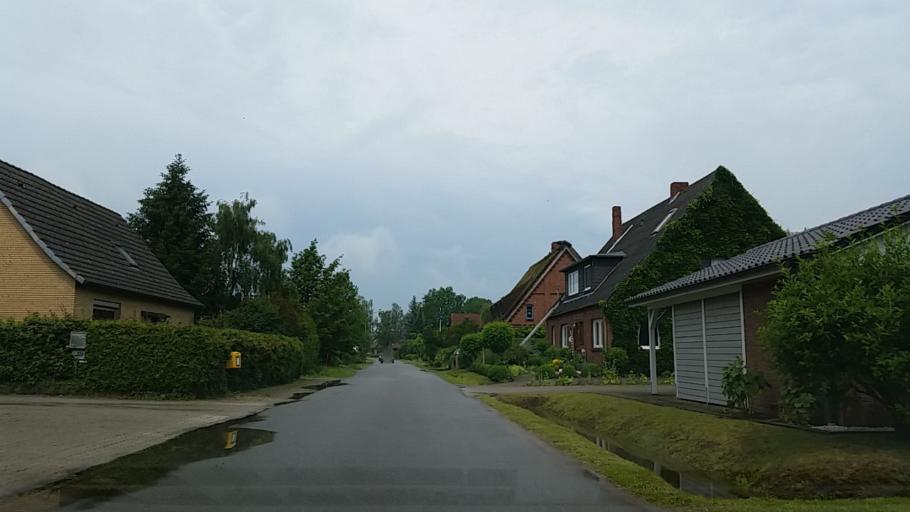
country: DE
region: Lower Saxony
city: Drage
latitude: 53.4168
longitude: 10.3142
